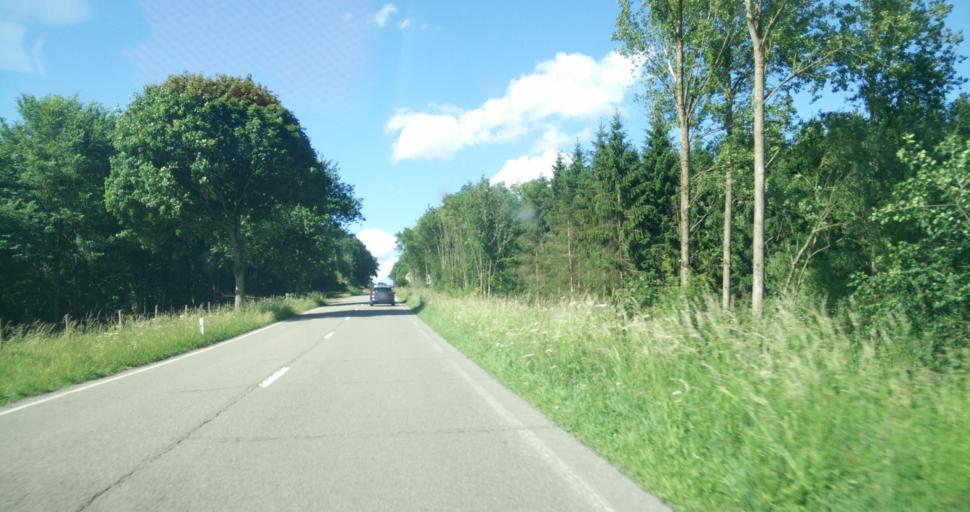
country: BE
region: Wallonia
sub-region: Province du Luxembourg
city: Marche-en-Famenne
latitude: 50.1991
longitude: 5.3668
